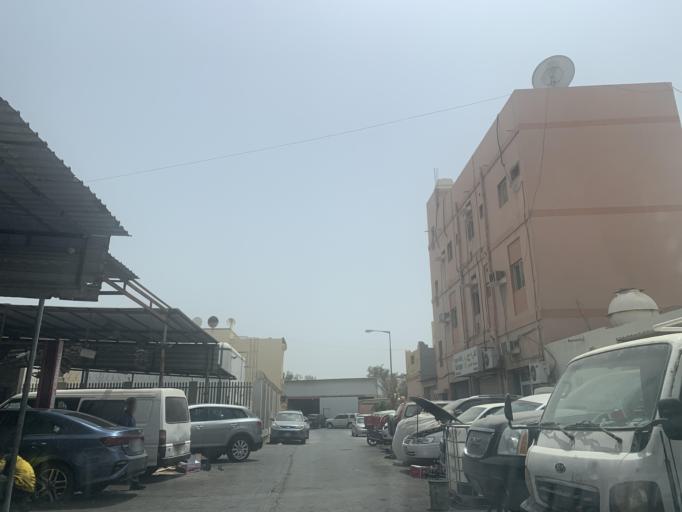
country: BH
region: Manama
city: Jidd Hafs
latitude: 26.2088
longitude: 50.5472
